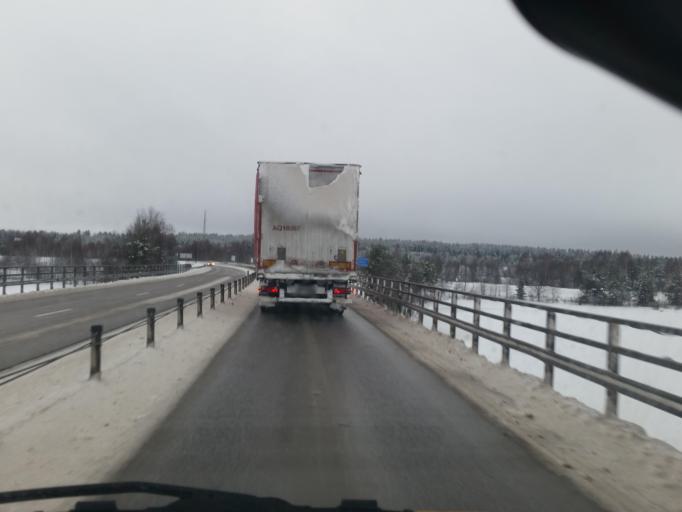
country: SE
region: Norrbotten
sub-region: Pitea Kommun
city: Bergsviken
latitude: 65.3140
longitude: 21.4101
